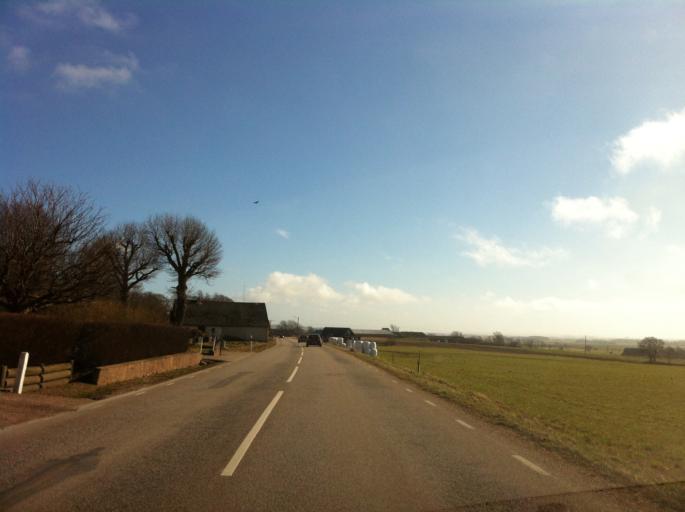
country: SE
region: Skane
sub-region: Bastads Kommun
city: Forslov
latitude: 56.3365
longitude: 12.8299
